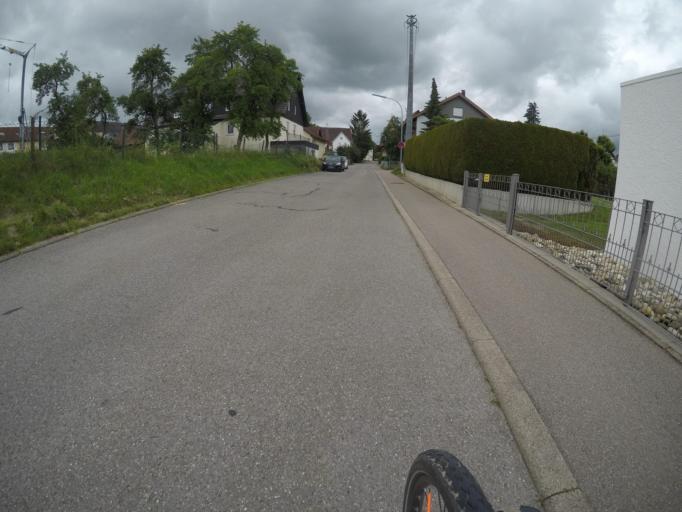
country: DE
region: Baden-Wuerttemberg
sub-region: Regierungsbezirk Stuttgart
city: Unterjettingen
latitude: 48.5676
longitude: 8.7841
